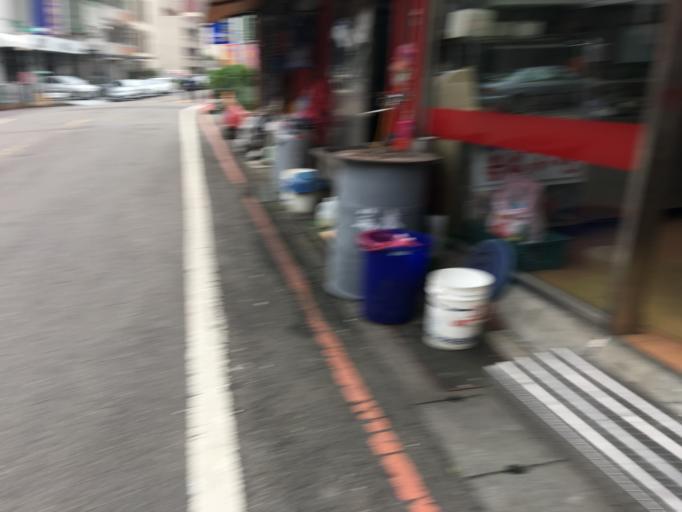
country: TW
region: Taiwan
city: Taoyuan City
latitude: 25.0170
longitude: 121.3027
